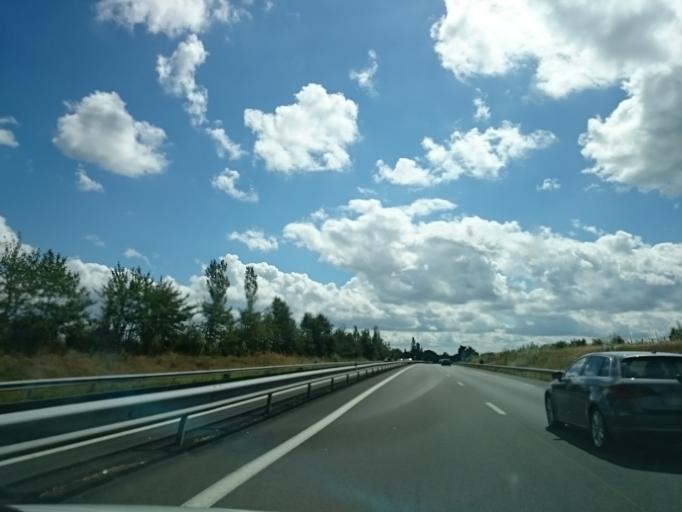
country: FR
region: Pays de la Loire
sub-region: Departement de Maine-et-Loire
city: Durtal
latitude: 47.6375
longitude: -0.2746
